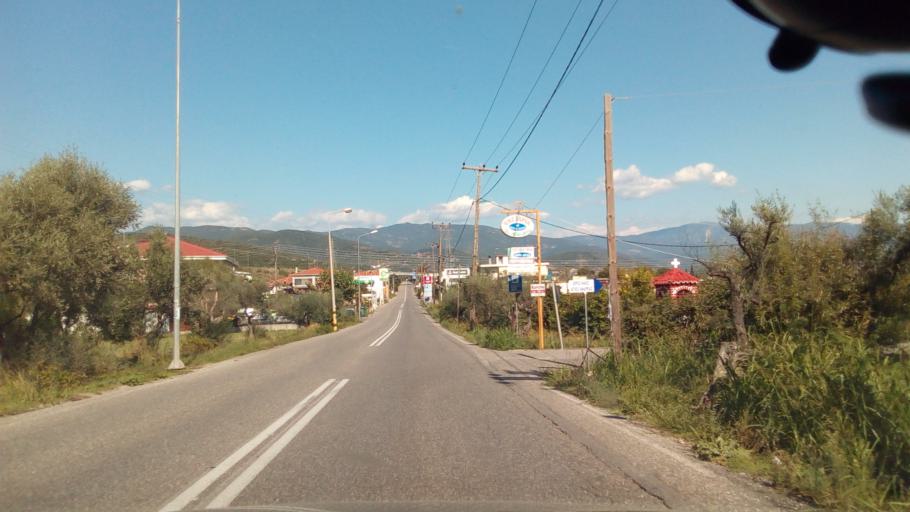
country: GR
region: West Greece
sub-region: Nomos Aitolias kai Akarnanias
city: Nafpaktos
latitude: 38.4038
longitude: 21.8608
